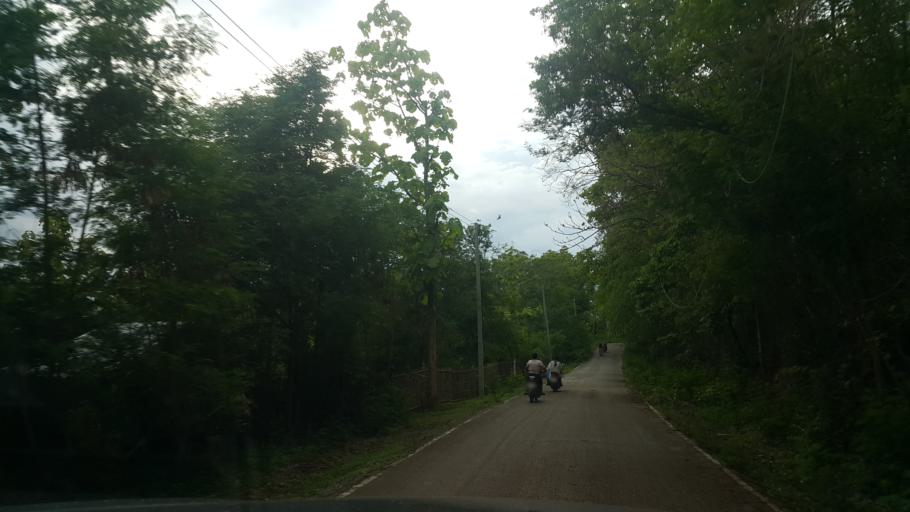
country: TH
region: Chiang Mai
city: Mae On
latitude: 18.7247
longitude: 99.2315
